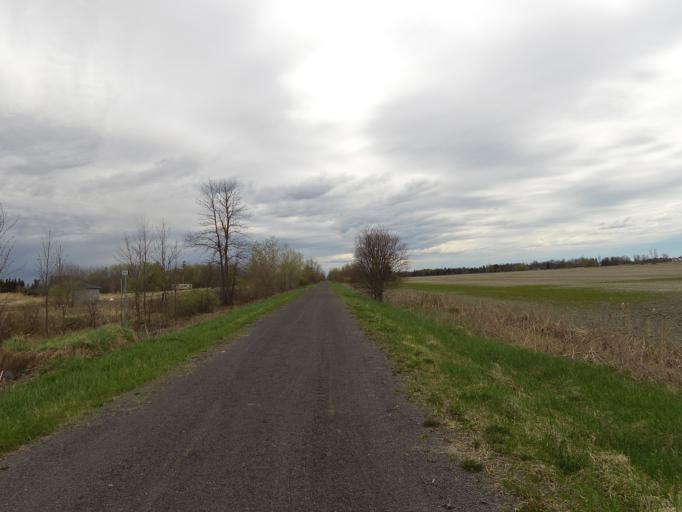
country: CA
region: Ontario
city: Hawkesbury
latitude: 45.5445
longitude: -74.7918
